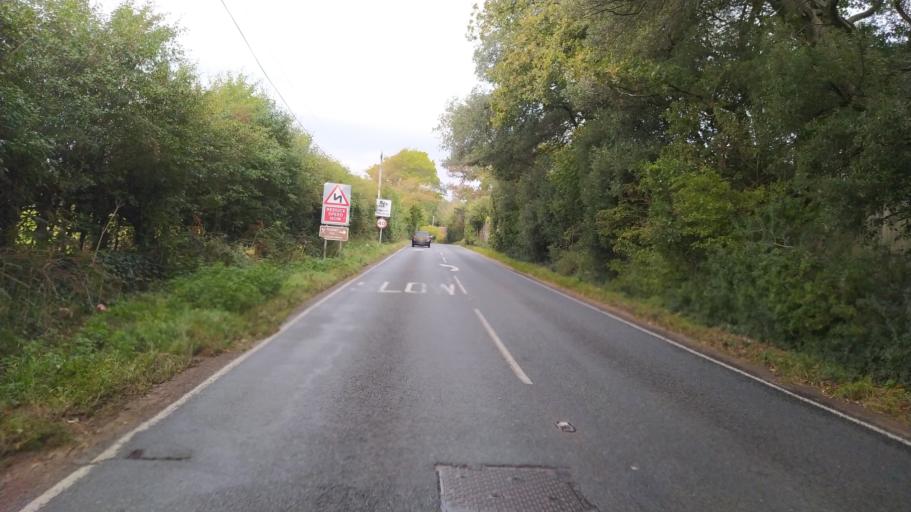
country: GB
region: England
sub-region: Hampshire
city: Brockenhurst
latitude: 50.7880
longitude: -1.5640
